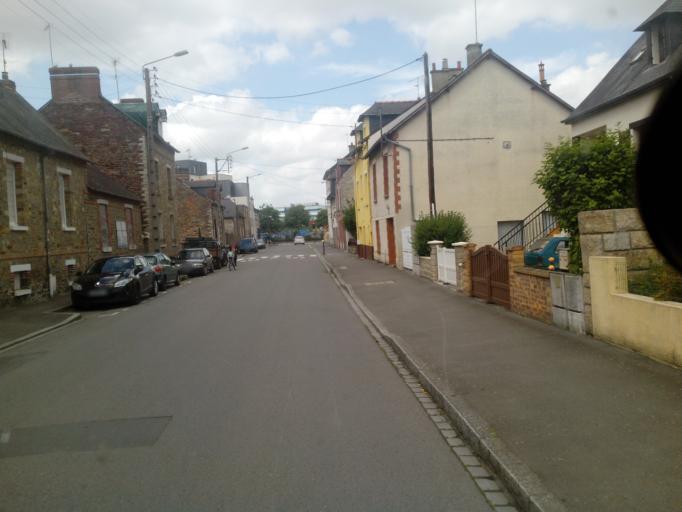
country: FR
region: Brittany
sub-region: Departement d'Ille-et-Vilaine
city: Rennes
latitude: 48.1041
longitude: -1.6999
